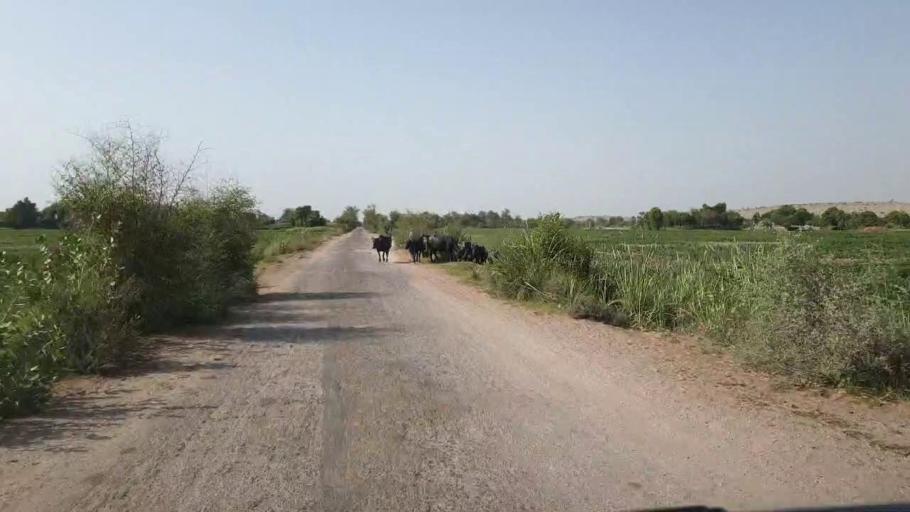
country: PK
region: Sindh
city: Kandiari
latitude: 26.6880
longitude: 68.9645
